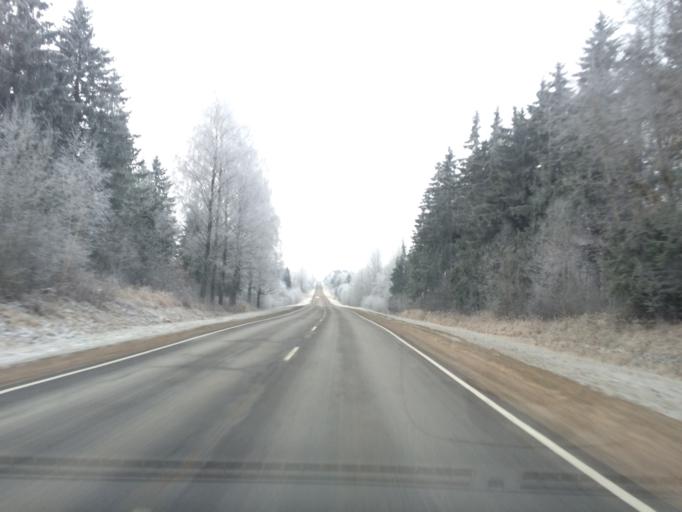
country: LV
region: Rezekne
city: Rezekne
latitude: 56.6285
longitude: 27.4629
